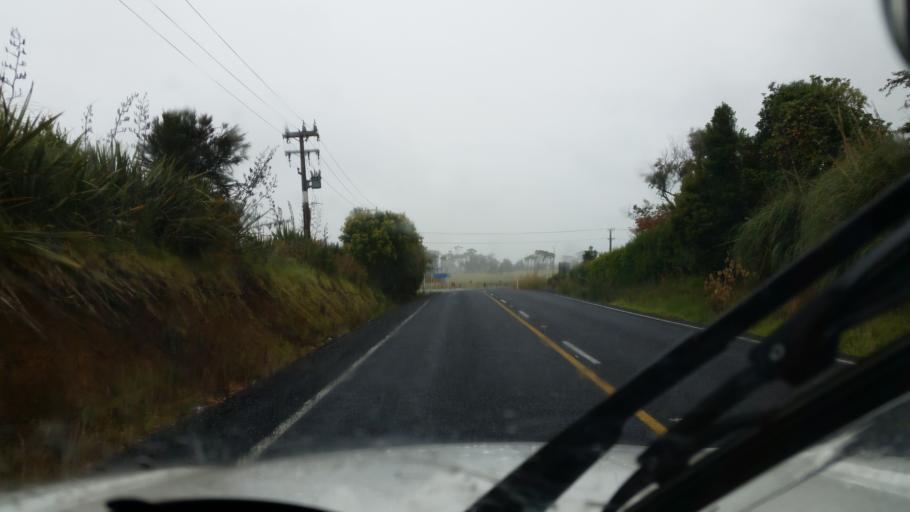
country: NZ
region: Northland
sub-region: Far North District
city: Ahipara
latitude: -35.1730
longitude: 173.1796
